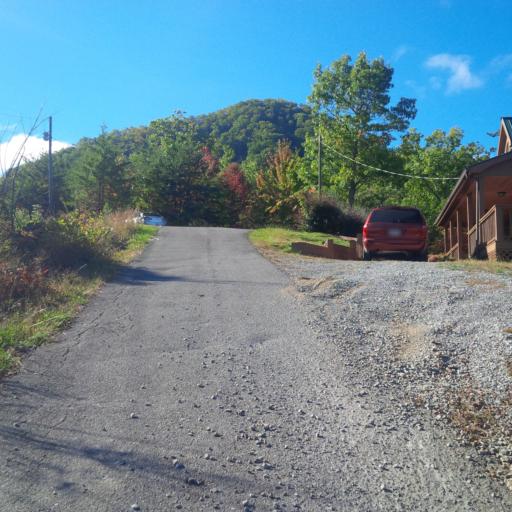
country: US
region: Tennessee
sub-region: Sevier County
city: Pigeon Forge
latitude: 35.6978
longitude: -83.6603
